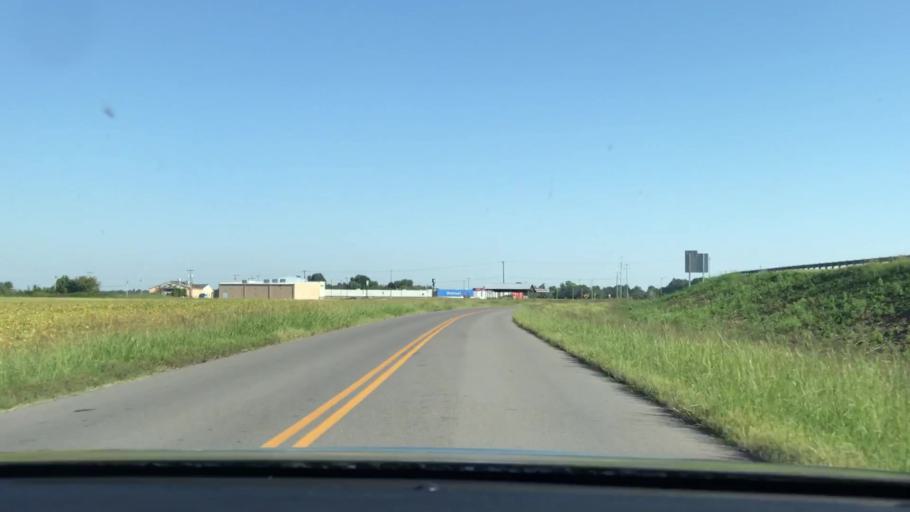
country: US
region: Kentucky
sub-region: Fulton County
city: Fulton
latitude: 36.5124
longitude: -88.9002
